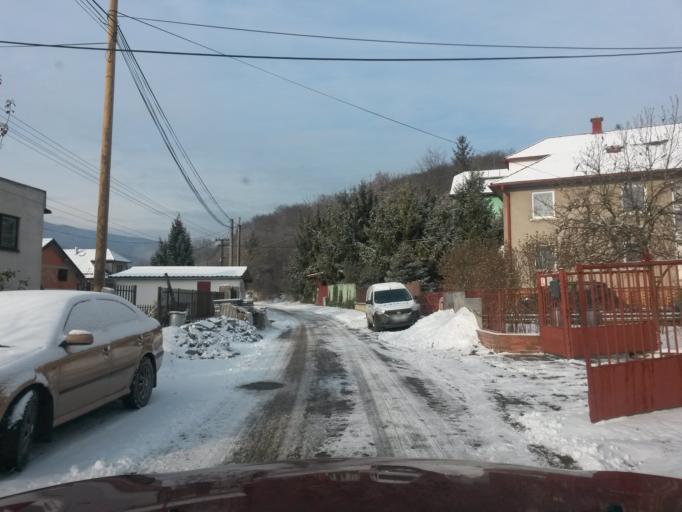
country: SK
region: Kosicky
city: Kosice
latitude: 48.8063
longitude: 21.2432
